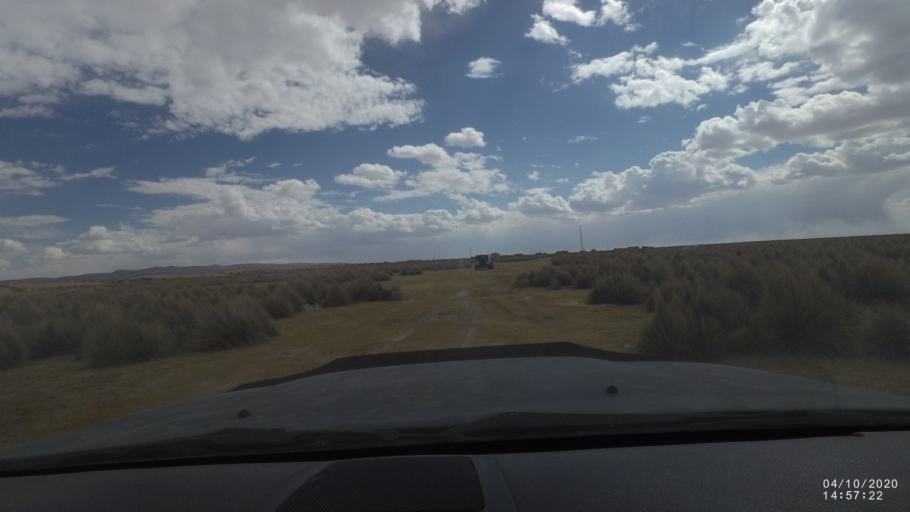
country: BO
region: Oruro
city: Poopo
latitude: -18.6854
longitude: -67.5186
